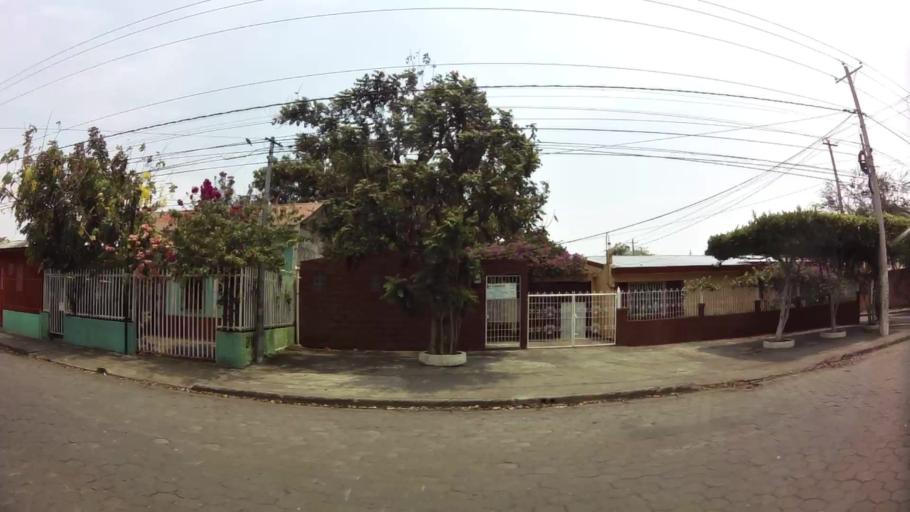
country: NI
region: Managua
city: Ciudad Sandino
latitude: 12.1452
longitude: -86.2987
